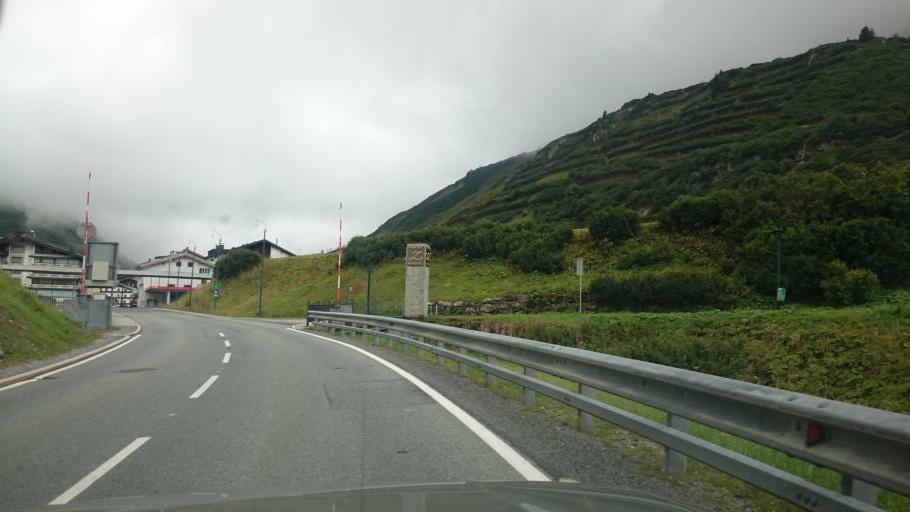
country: AT
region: Vorarlberg
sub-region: Politischer Bezirk Bludenz
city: Lech
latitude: 47.1729
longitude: 10.1624
